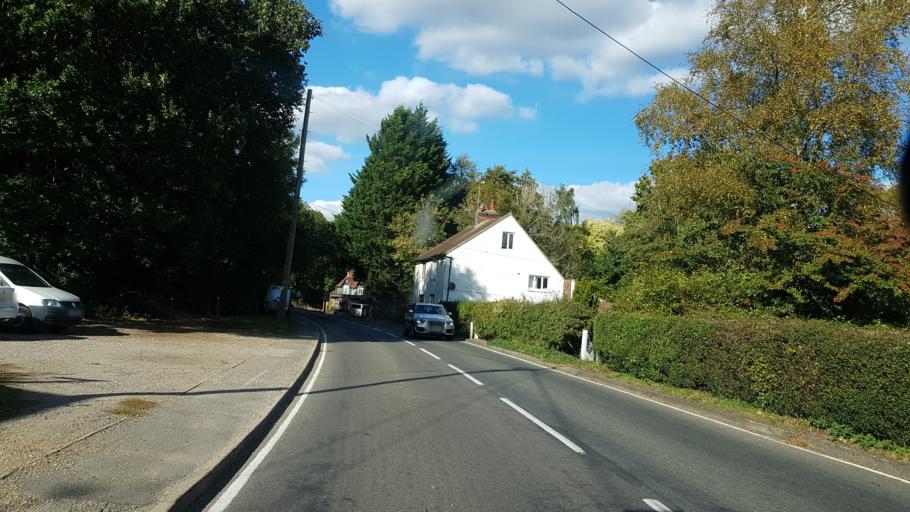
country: GB
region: England
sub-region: Surrey
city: Chiddingfold
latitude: 51.1188
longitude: -0.6228
